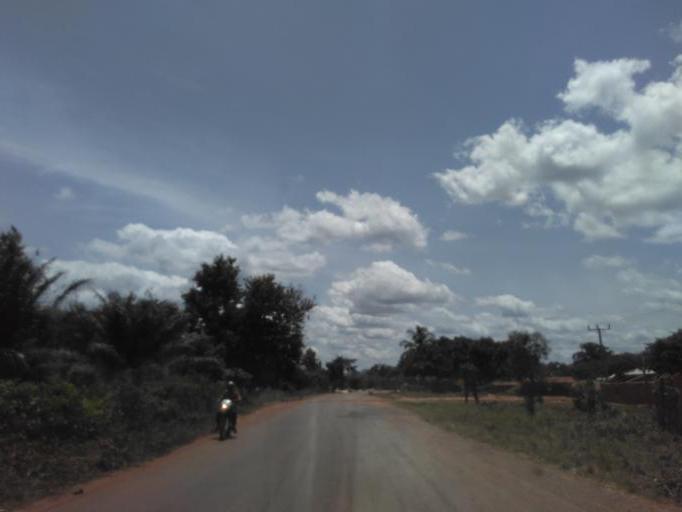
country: GH
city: Akropong
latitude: 6.0938
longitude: -0.1011
